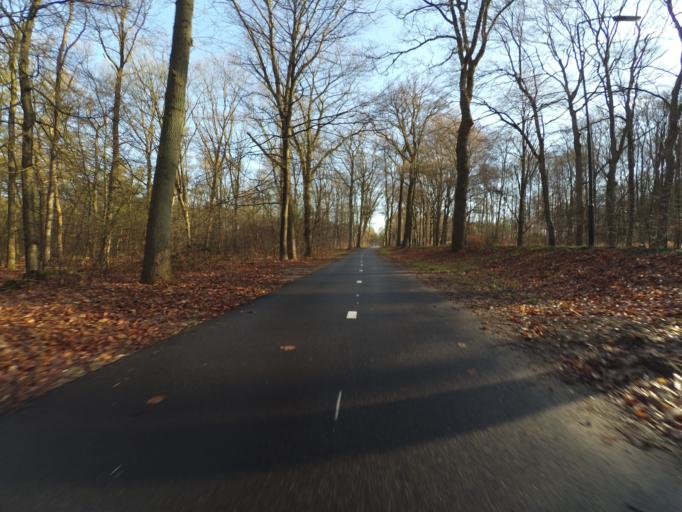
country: NL
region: Gelderland
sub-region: Gemeente Apeldoorn
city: Beekbergen
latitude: 52.1224
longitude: 5.8732
